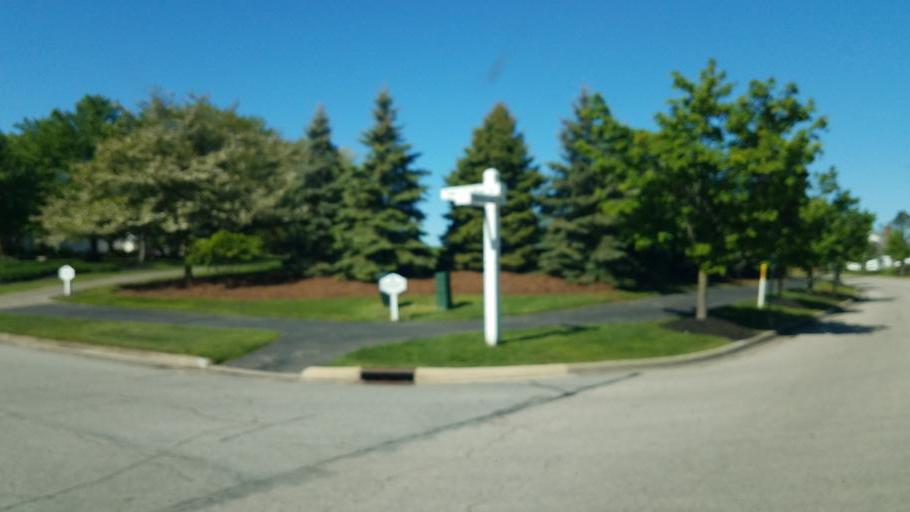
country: US
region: Ohio
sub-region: Franklin County
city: Westerville
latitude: 40.1653
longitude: -82.9360
